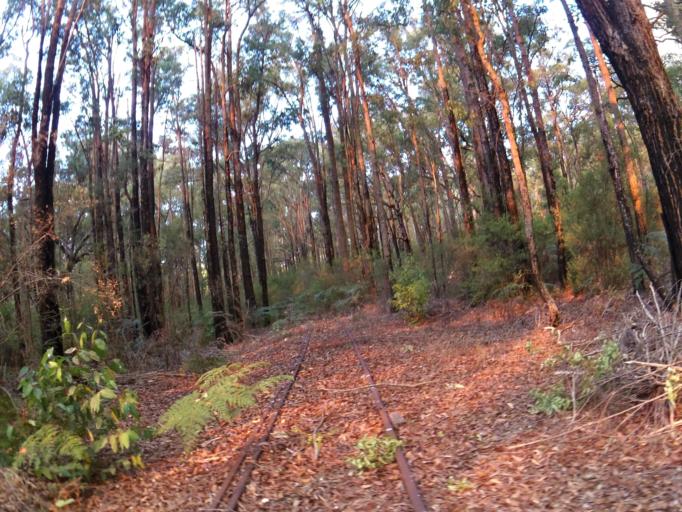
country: AU
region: Western Australia
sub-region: Waroona
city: Waroona
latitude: -32.7403
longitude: 116.1430
